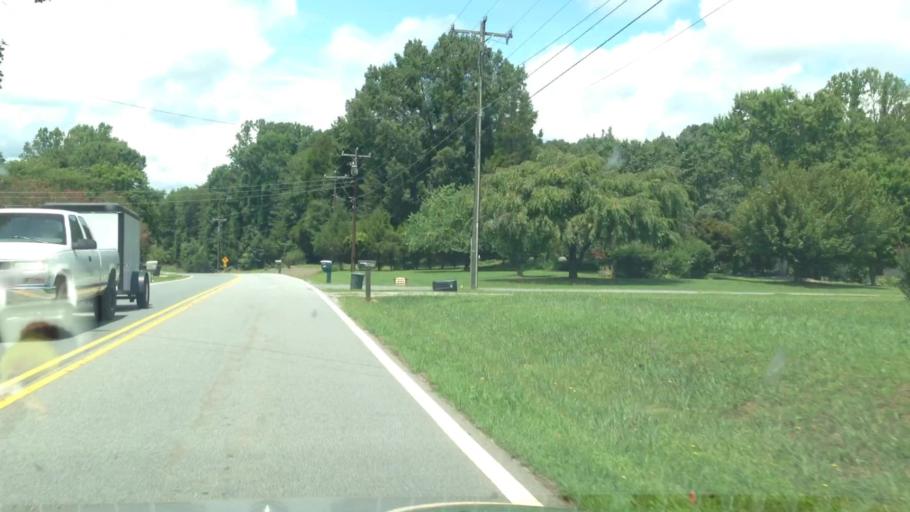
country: US
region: North Carolina
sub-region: Forsyth County
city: Kernersville
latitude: 36.1494
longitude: -80.0892
